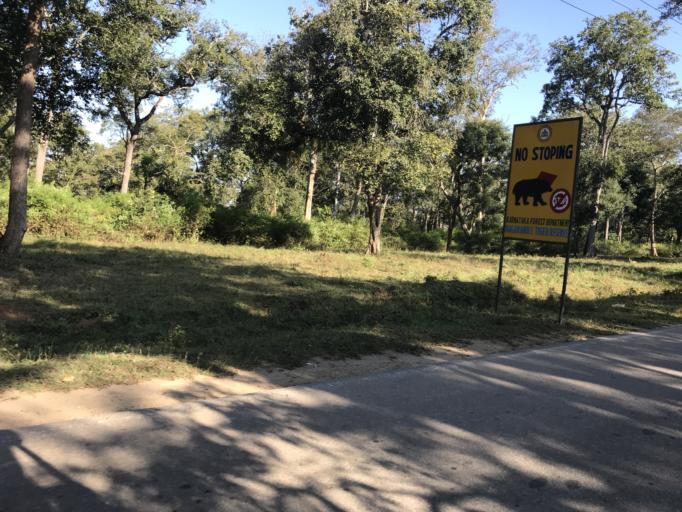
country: IN
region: Karnataka
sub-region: Mysore
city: Heggadadevankote
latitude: 11.9530
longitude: 76.2283
